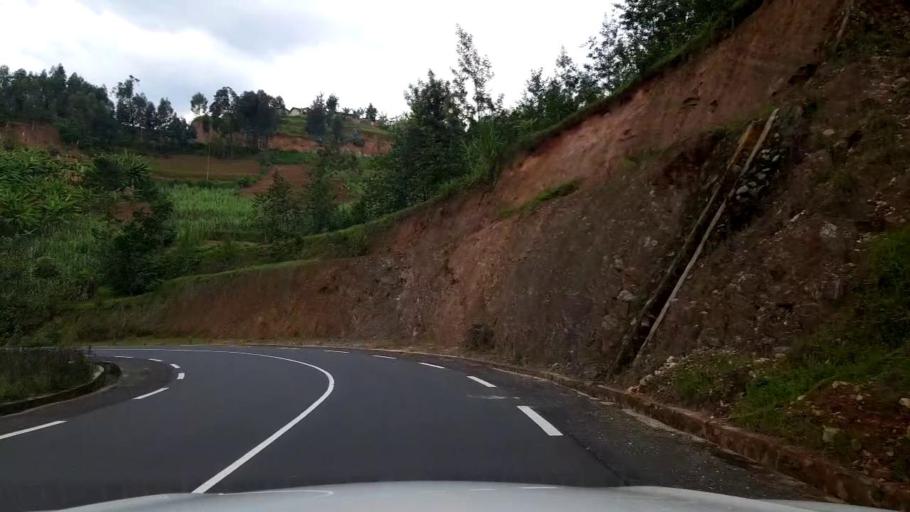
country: RW
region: Western Province
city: Kibuye
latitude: -1.9068
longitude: 29.3647
